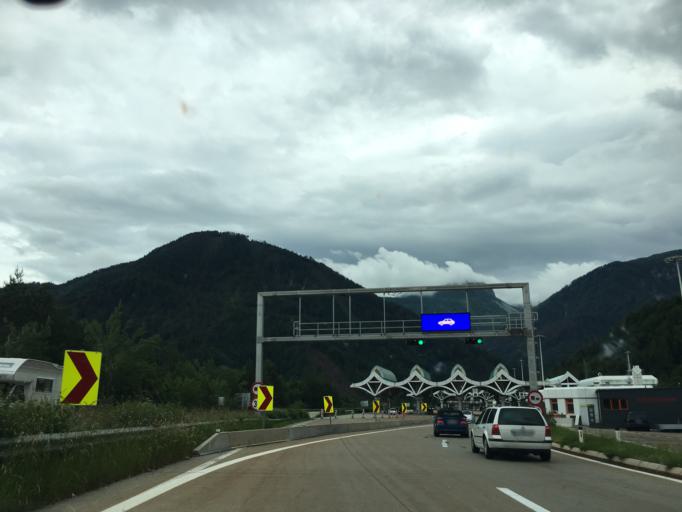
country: AT
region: Carinthia
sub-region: Politischer Bezirk Villach Land
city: Sankt Jakob
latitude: 46.5319
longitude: 14.0310
